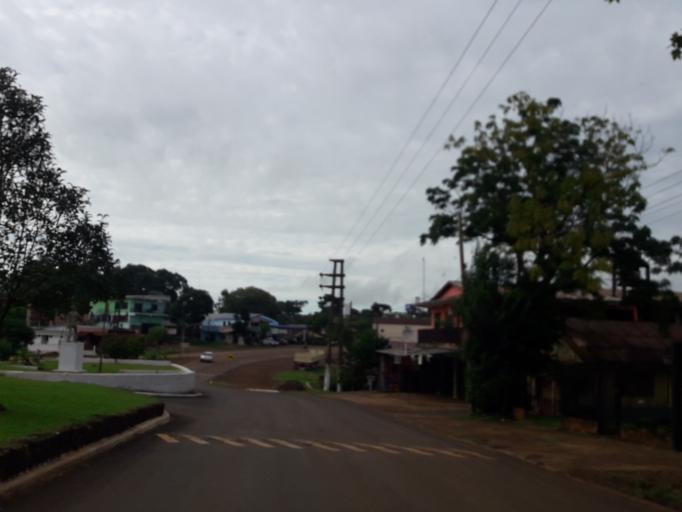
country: AR
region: Misiones
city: Bernardo de Irigoyen
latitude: -26.2590
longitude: -53.6476
